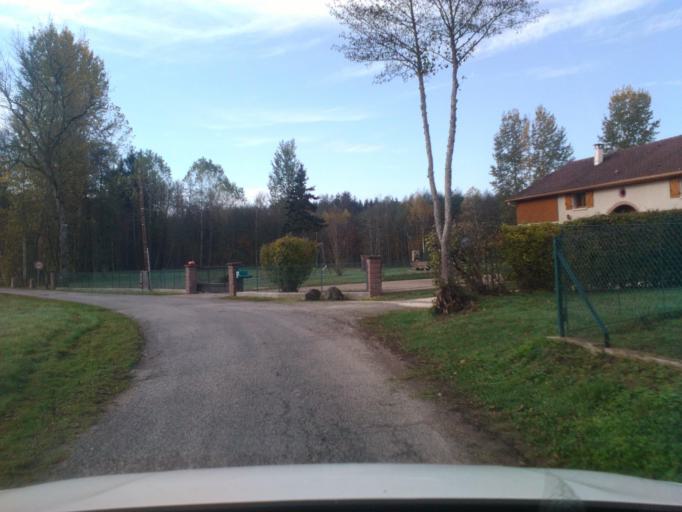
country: FR
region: Lorraine
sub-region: Departement des Vosges
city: Saint-Michel-sur-Meurthe
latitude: 48.3489
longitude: 6.8986
